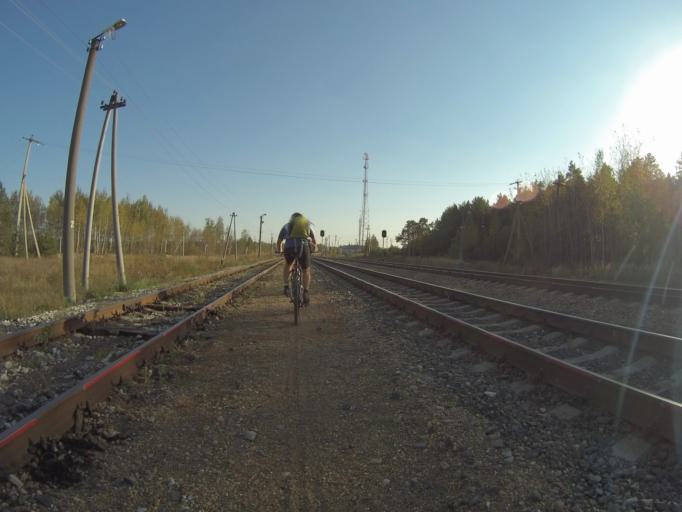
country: RU
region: Vladimir
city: Raduzhnyy
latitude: 56.0246
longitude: 40.3859
